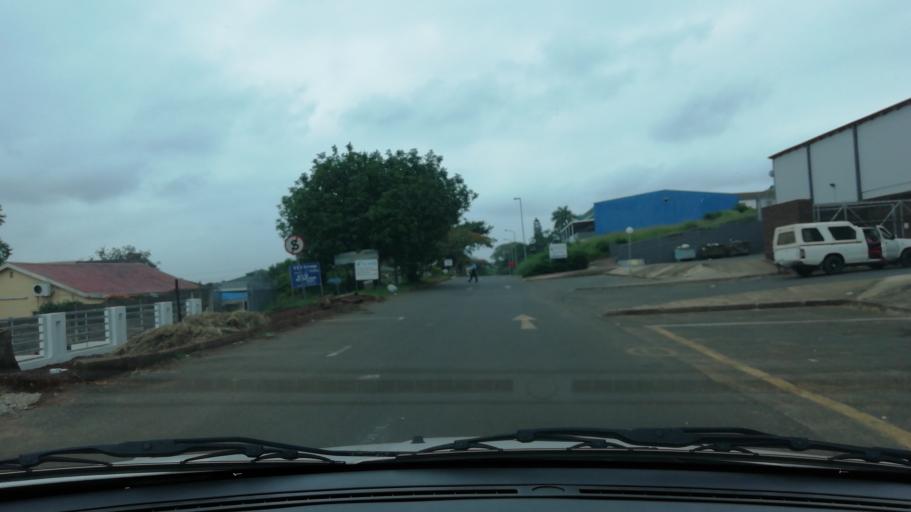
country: ZA
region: KwaZulu-Natal
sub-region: uThungulu District Municipality
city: Empangeni
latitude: -28.7387
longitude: 31.8928
